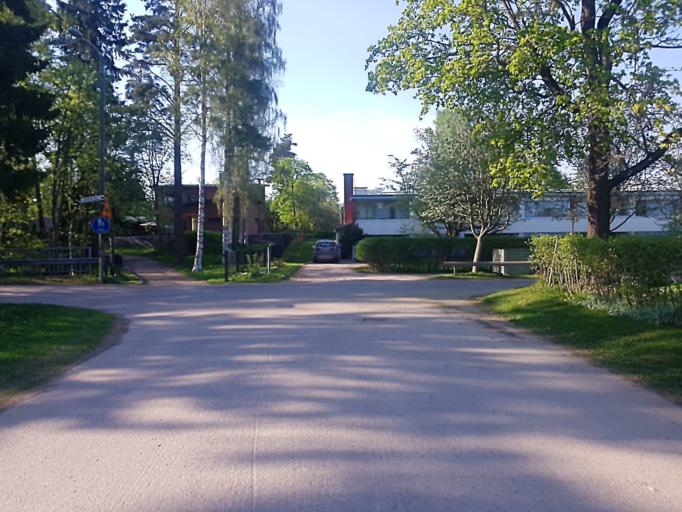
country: FI
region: Uusimaa
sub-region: Helsinki
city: Helsinki
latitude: 60.2349
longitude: 24.9214
